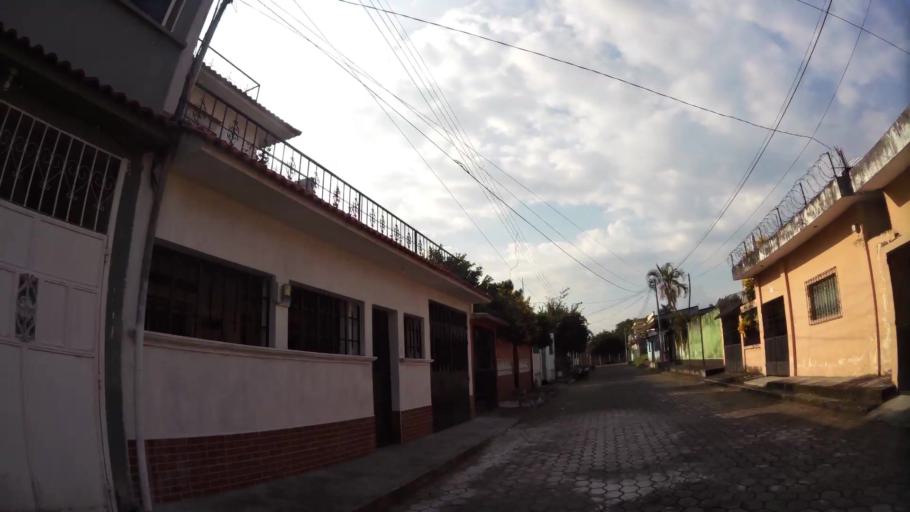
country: GT
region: Retalhuleu
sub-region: Municipio de Retalhuleu
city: Retalhuleu
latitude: 14.5438
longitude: -91.6732
